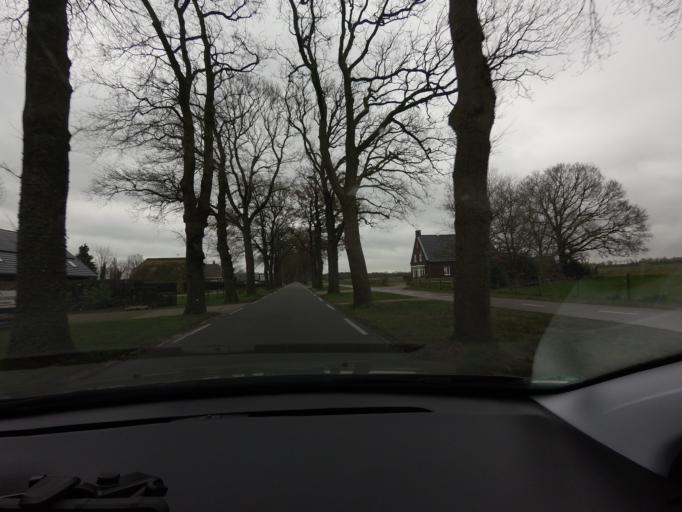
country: NL
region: Drenthe
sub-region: Gemeente Assen
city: Assen
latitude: 52.8537
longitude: 6.5738
